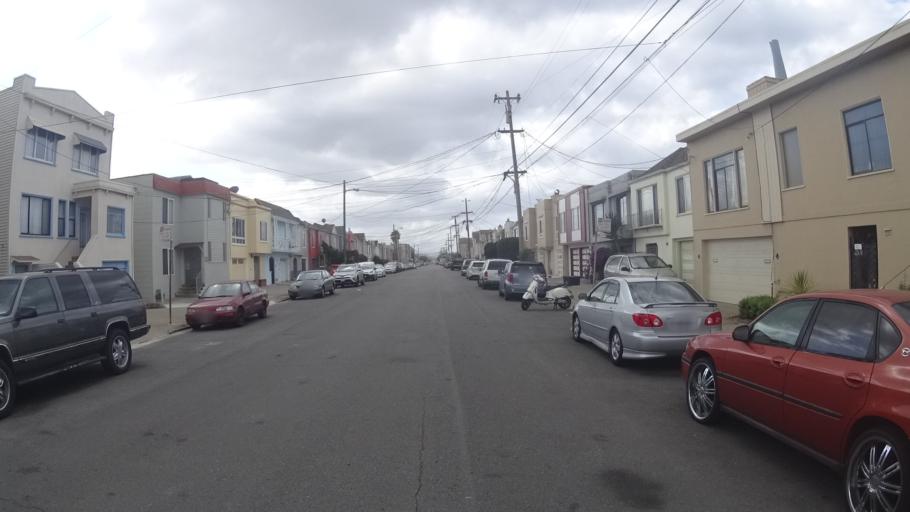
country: US
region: California
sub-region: San Mateo County
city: Daly City
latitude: 37.7546
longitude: -122.5077
